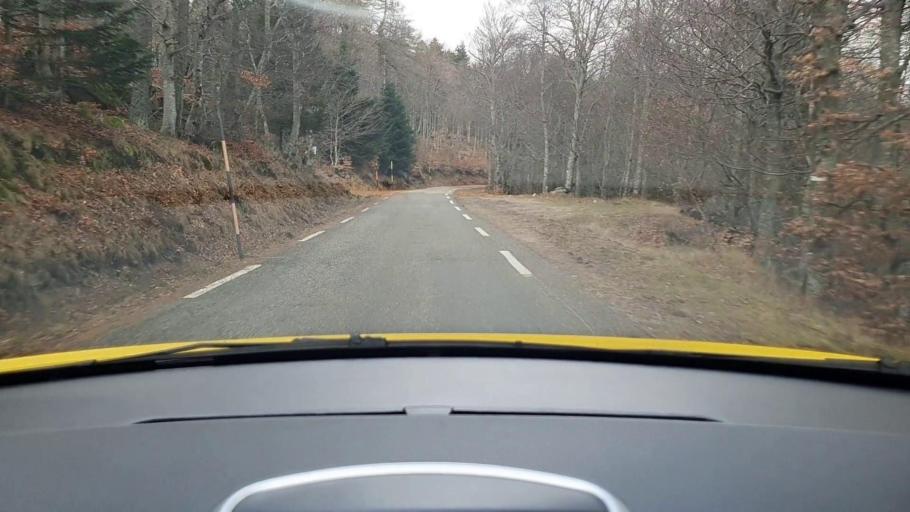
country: FR
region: Languedoc-Roussillon
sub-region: Departement du Gard
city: Branoux-les-Taillades
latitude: 44.3753
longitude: 3.9123
